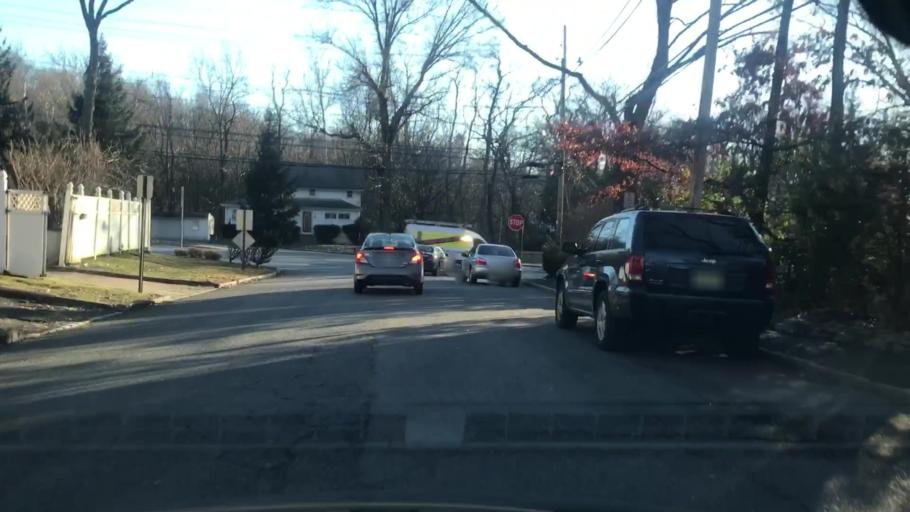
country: US
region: New Jersey
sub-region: Essex County
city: Northfield
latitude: 40.7720
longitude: -74.3084
